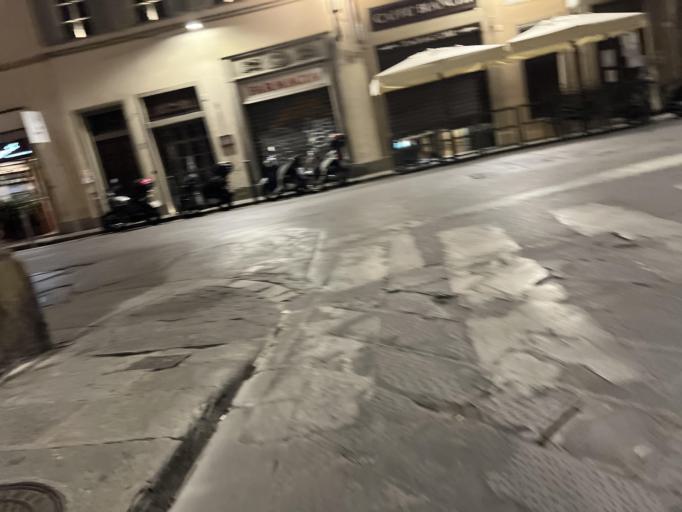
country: IT
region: Tuscany
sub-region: Province of Florence
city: Florence
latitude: 43.7651
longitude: 11.2479
